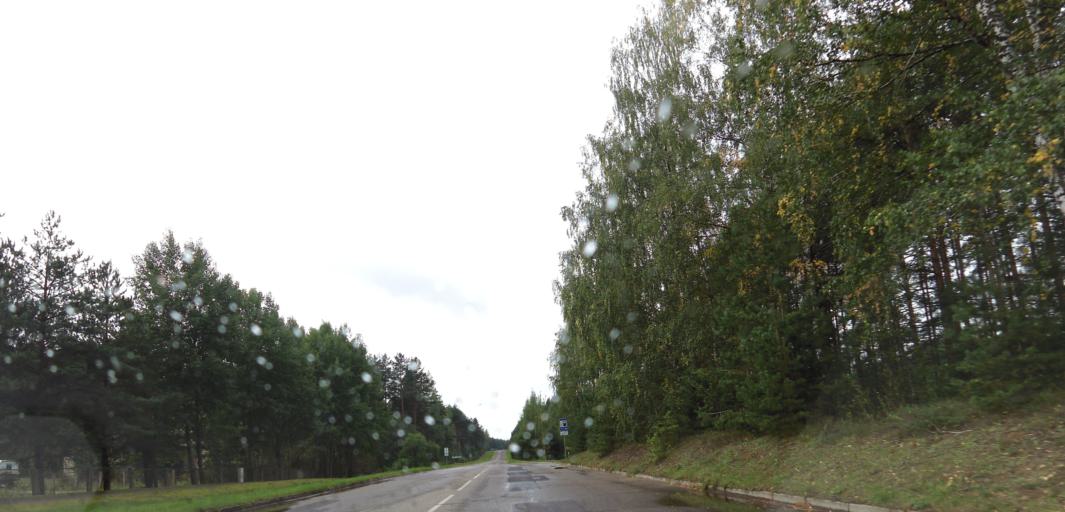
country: LT
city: Moletai
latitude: 55.2229
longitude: 25.3968
